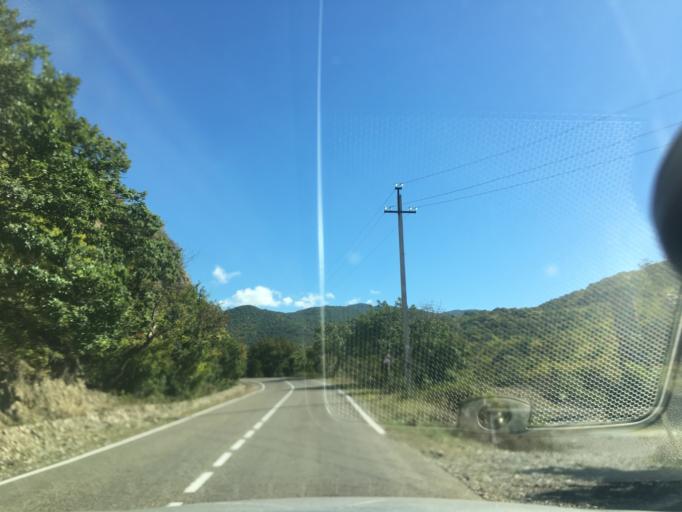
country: GE
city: Zahesi
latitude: 41.8399
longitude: 44.8727
